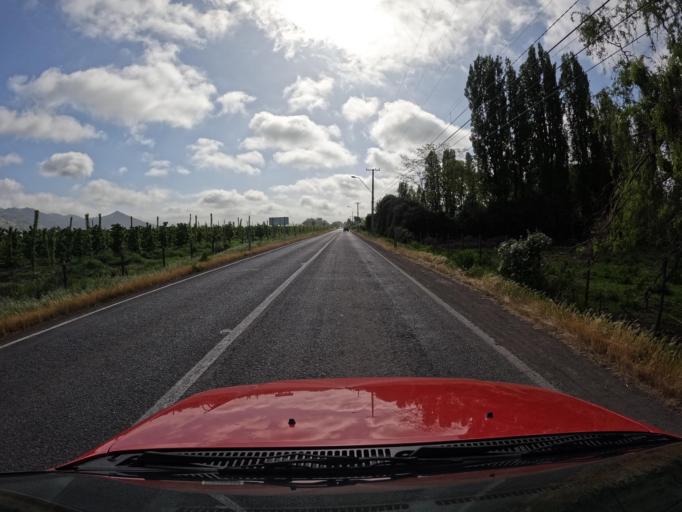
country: CL
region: Maule
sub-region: Provincia de Curico
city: Teno
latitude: -34.8725
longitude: -71.2246
